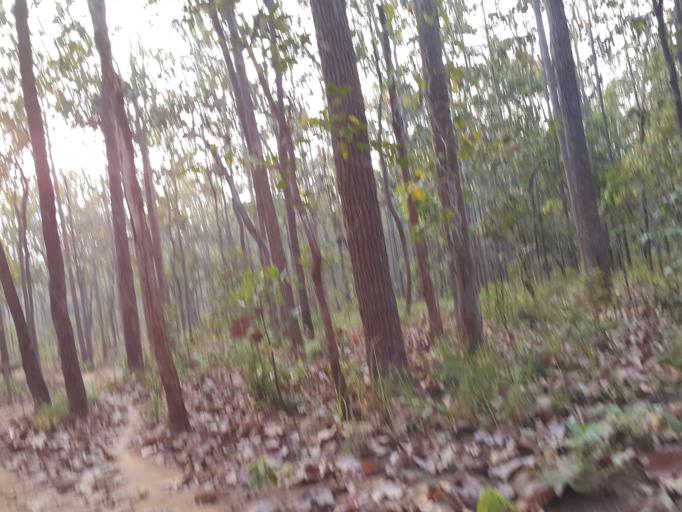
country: TH
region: Lamphun
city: Li
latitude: 17.6136
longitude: 98.8785
